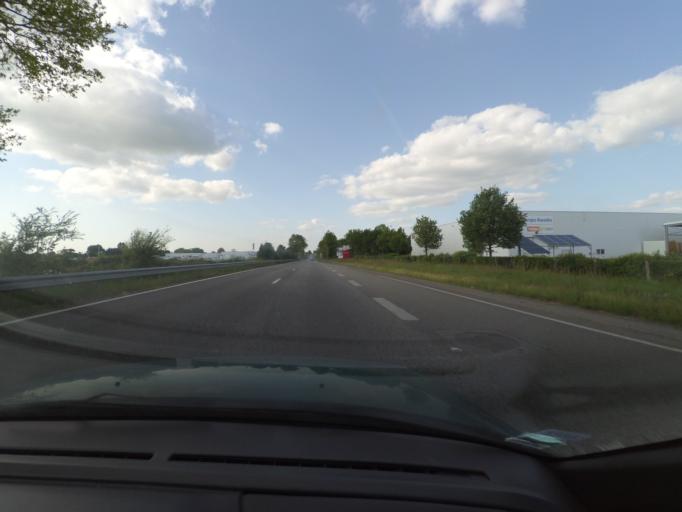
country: FR
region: Pays de la Loire
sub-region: Departement de la Vendee
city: Belleville-sur-Vie
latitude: 46.7470
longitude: -1.4304
